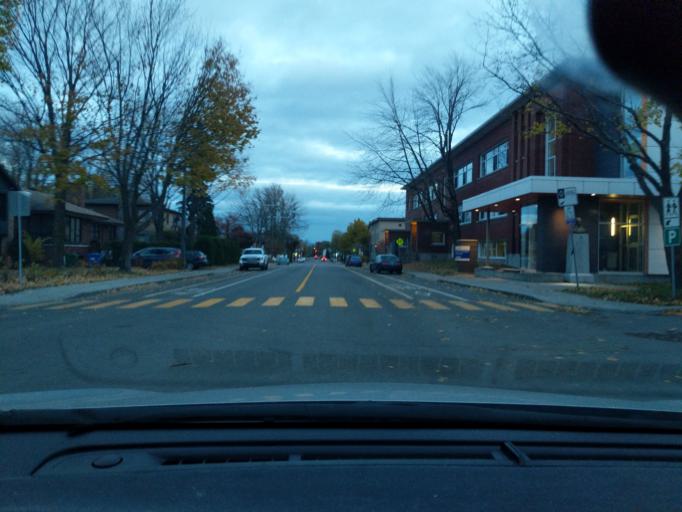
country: CA
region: Quebec
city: Quebec
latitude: 46.7860
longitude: -71.2499
